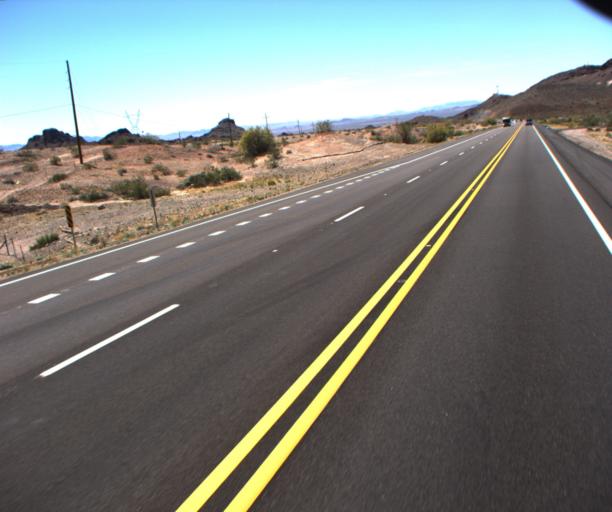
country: US
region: Arizona
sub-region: Mohave County
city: Desert Hills
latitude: 34.6092
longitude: -114.3569
